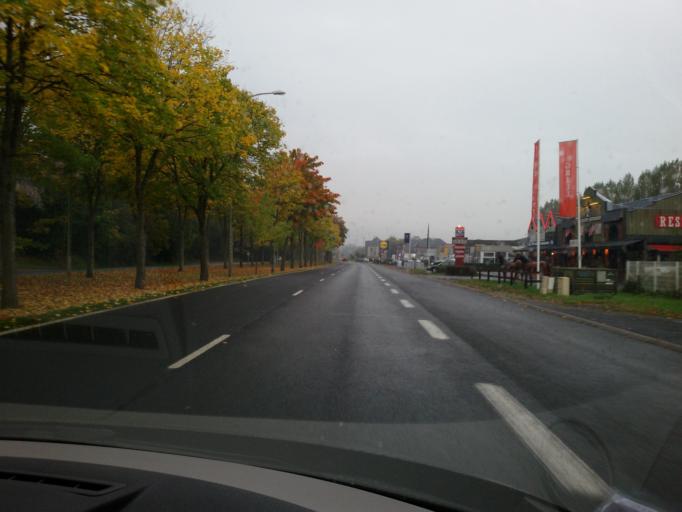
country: FR
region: Lower Normandy
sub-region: Departement du Calvados
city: Honfleur
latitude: 49.4144
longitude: 0.2473
